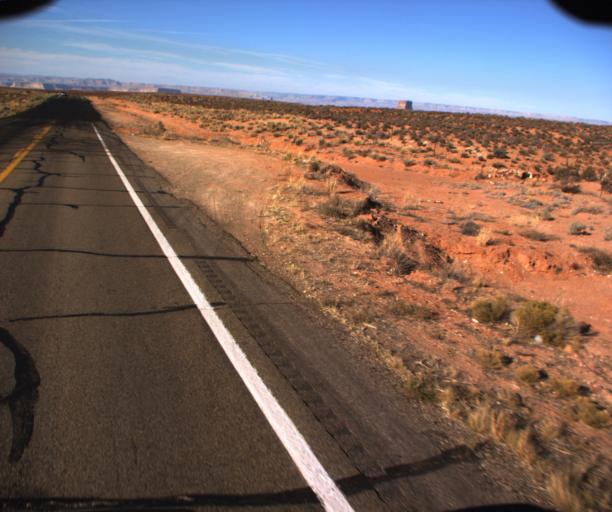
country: US
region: Arizona
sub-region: Coconino County
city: LeChee
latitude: 36.8721
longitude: -111.3421
